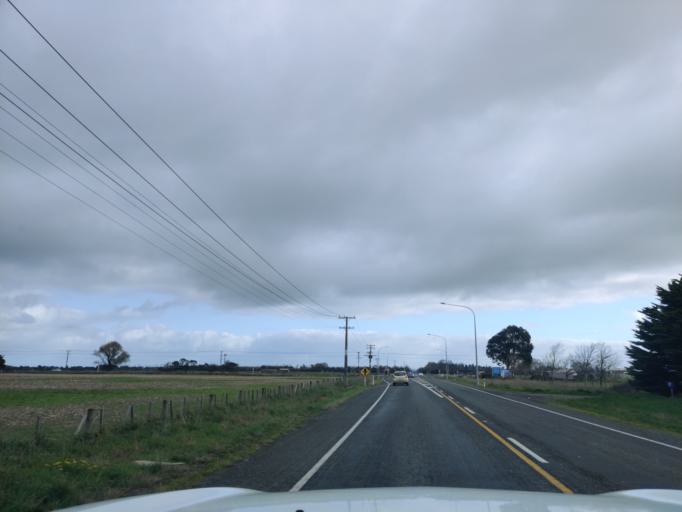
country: NZ
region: Manawatu-Wanganui
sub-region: Palmerston North City
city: Palmerston North
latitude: -40.3342
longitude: 175.5921
